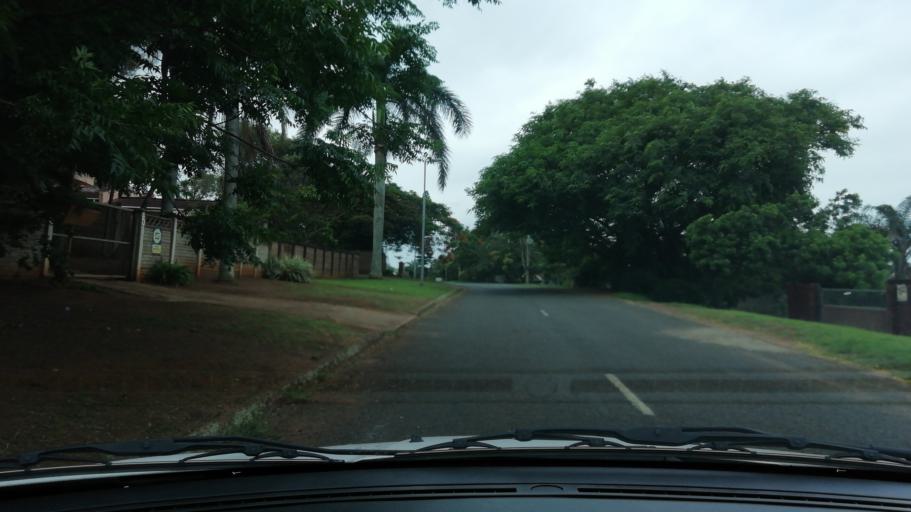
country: ZA
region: KwaZulu-Natal
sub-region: uThungulu District Municipality
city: Empangeni
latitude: -28.7369
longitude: 31.9024
